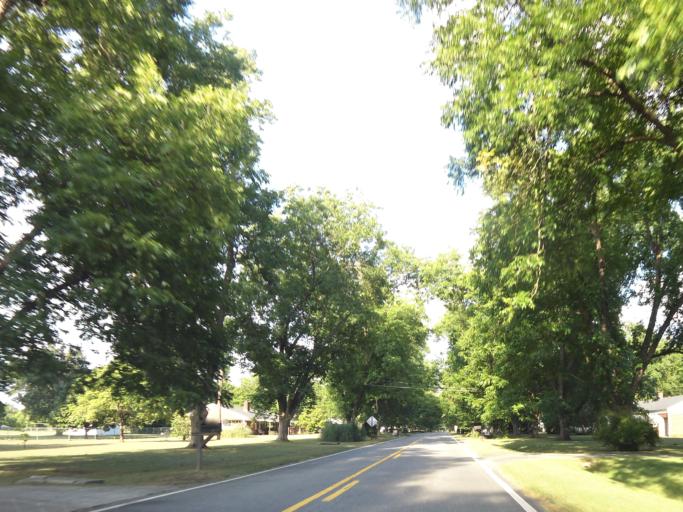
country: US
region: Georgia
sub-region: Houston County
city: Centerville
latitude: 32.7083
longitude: -83.6786
